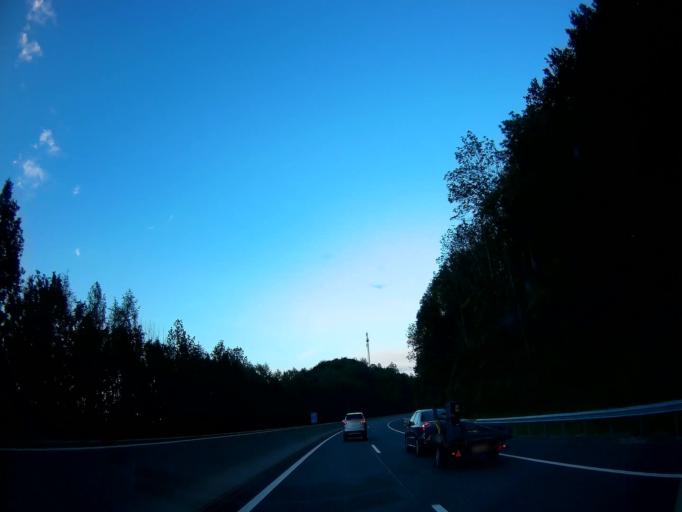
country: AT
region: Lower Austria
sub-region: Politischer Bezirk Wien-Umgebung
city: Pressbaum
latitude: 48.1787
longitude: 16.0873
